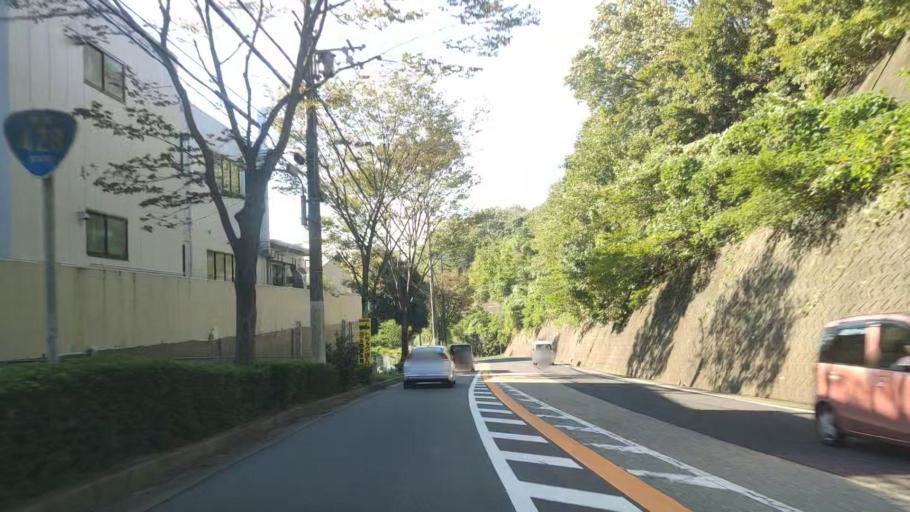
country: JP
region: Hyogo
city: Kobe
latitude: 34.7364
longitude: 135.1586
